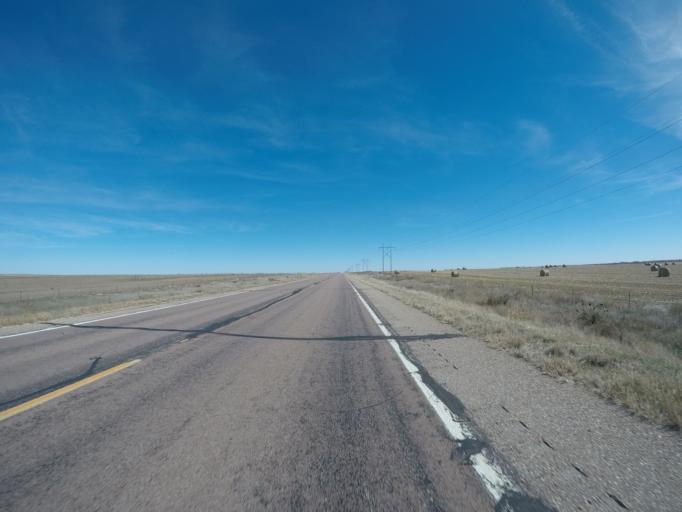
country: US
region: Colorado
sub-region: Yuma County
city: Yuma
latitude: 39.6548
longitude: -102.7982
